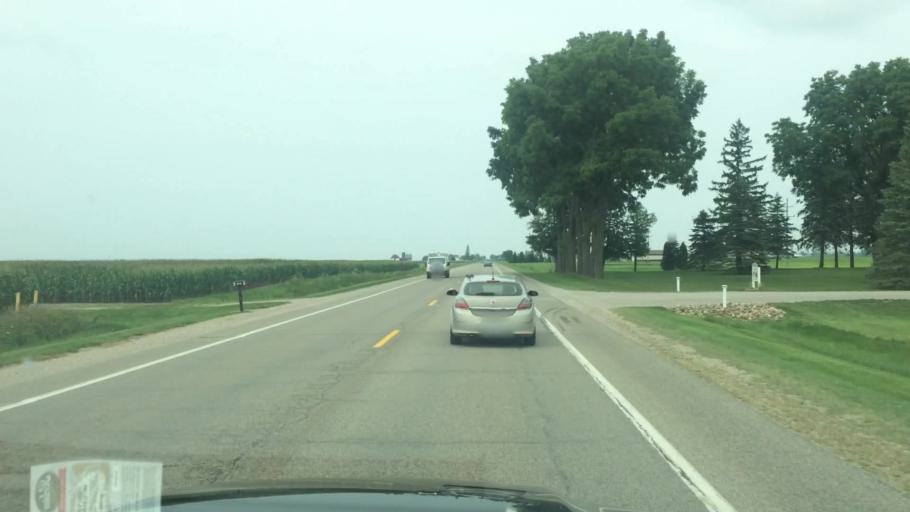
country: US
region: Michigan
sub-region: Huron County
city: Bad Axe
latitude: 43.9040
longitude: -83.0037
